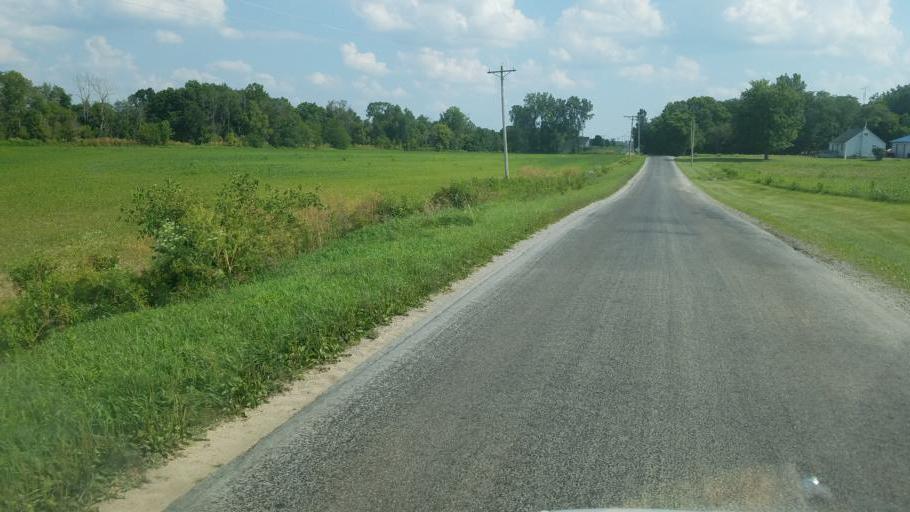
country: US
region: Ohio
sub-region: Hardin County
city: Kenton
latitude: 40.5821
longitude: -83.4545
